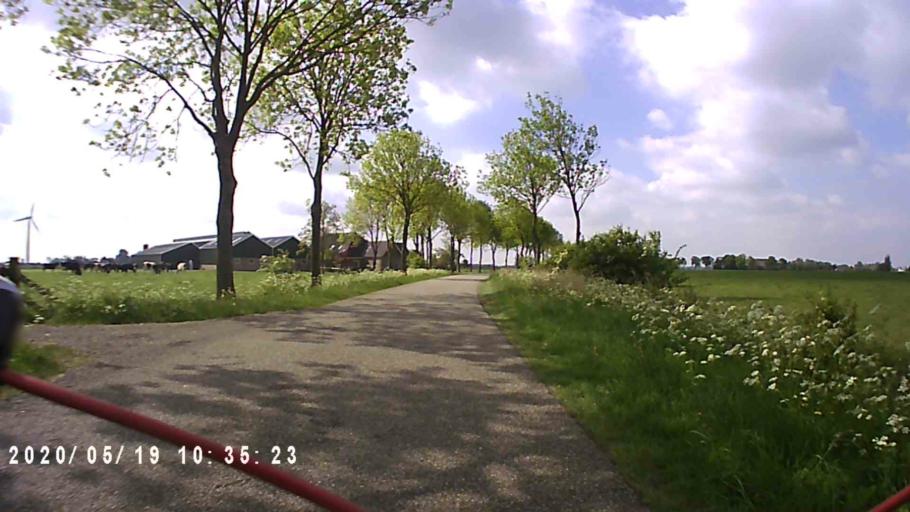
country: NL
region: Friesland
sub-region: Gemeente Kollumerland en Nieuwkruisland
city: Kollum
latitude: 53.2813
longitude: 6.1850
